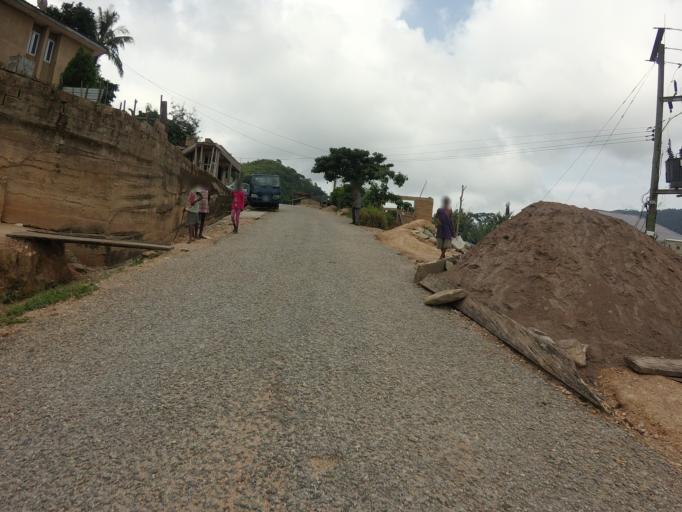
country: TG
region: Plateaux
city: Kpalime
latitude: 6.8888
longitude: 0.4557
